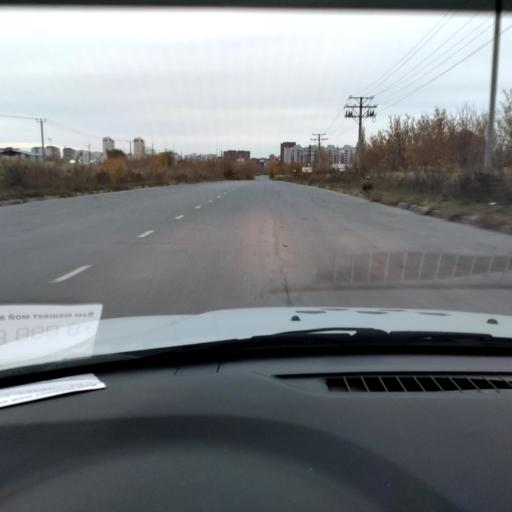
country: RU
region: Samara
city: Tol'yatti
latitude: 53.5551
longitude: 49.3284
